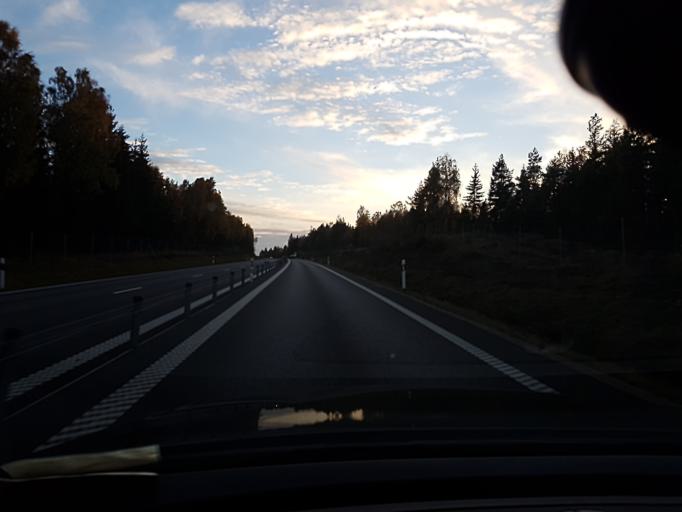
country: SE
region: Kronoberg
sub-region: Ljungby Kommun
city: Ljungby
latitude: 56.7845
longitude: 13.8253
